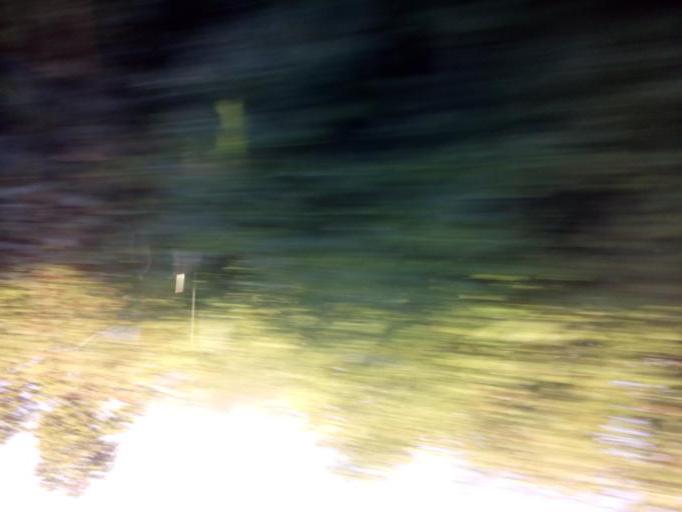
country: GB
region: England
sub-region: Gateshead
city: Lamesley
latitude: 54.9345
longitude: -1.6097
